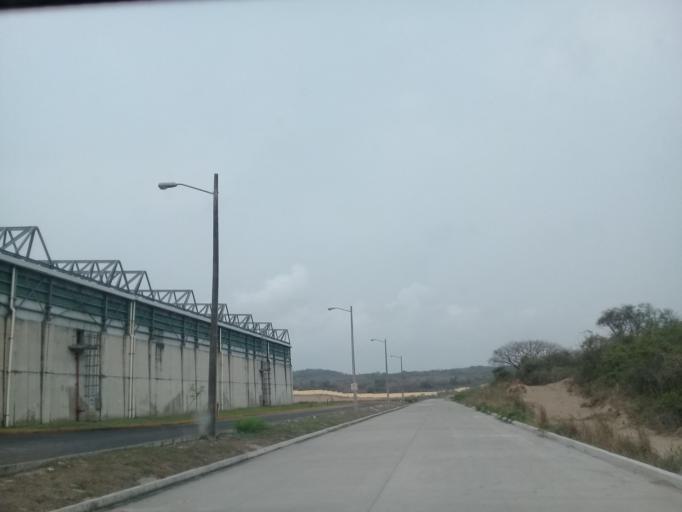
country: MX
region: Veracruz
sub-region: Veracruz
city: Colonia el Renacimiento
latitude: 19.2310
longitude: -96.1966
